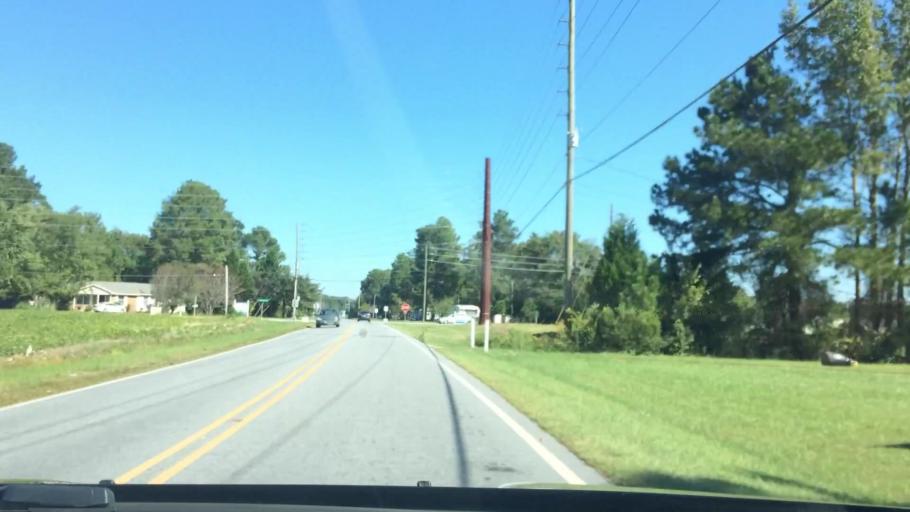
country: US
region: North Carolina
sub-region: Pitt County
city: Summerfield
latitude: 35.6106
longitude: -77.4270
